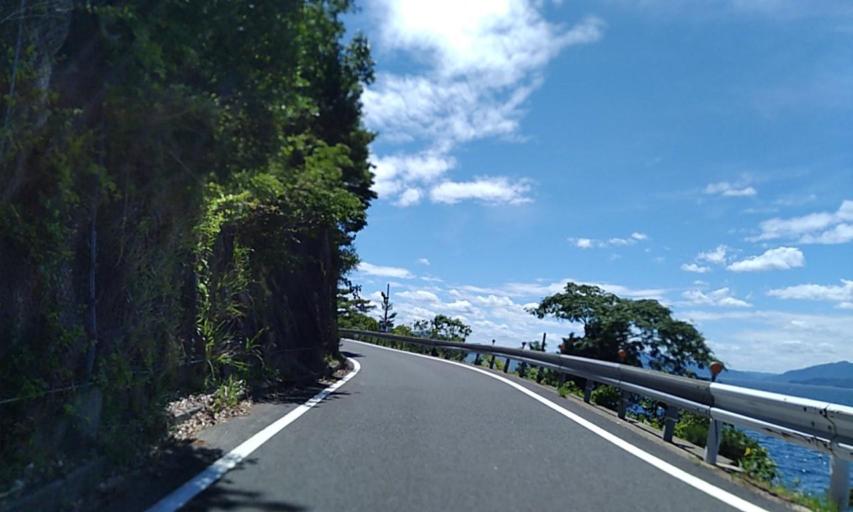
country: JP
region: Kyoto
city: Miyazu
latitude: 35.6672
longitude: 135.2712
